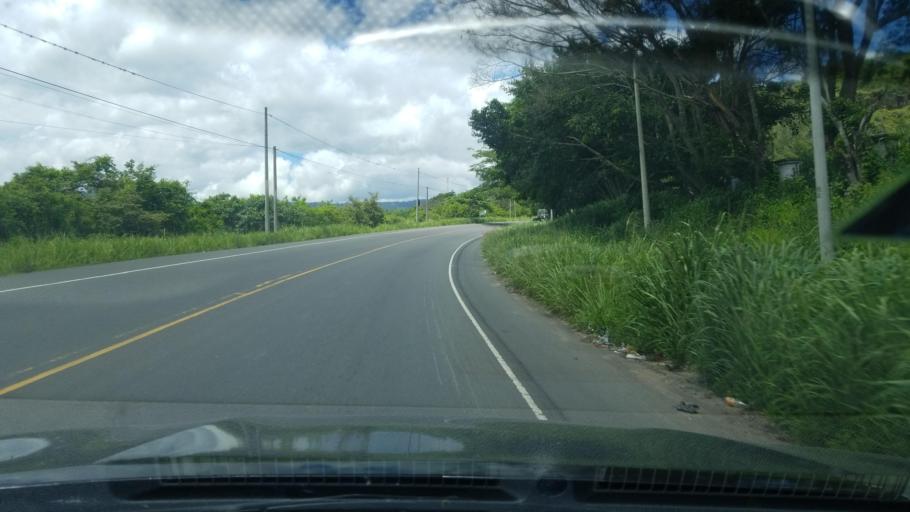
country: HN
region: Francisco Morazan
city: Cofradia
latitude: 14.1972
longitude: -87.2068
